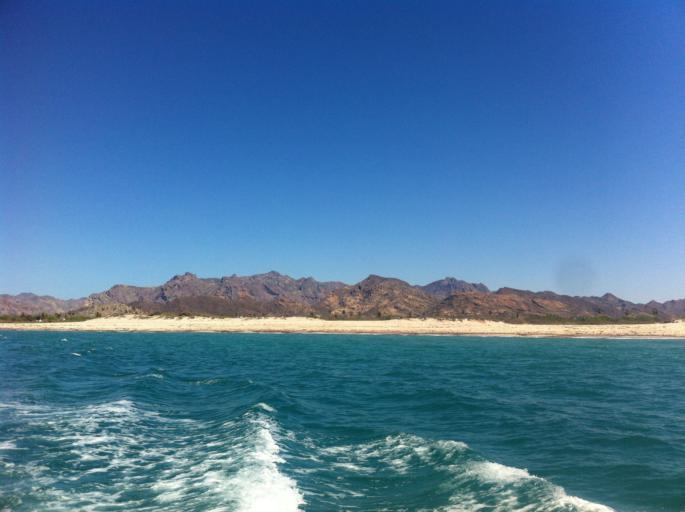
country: MX
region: Sonora
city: Heroica Guaymas
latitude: 27.9627
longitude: -111.0055
